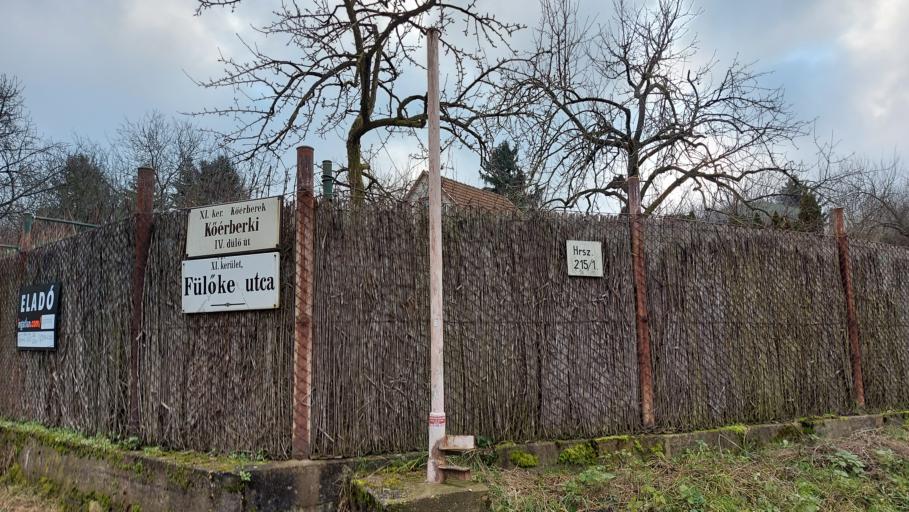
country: HU
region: Pest
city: Budaors
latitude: 47.4436
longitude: 18.9925
